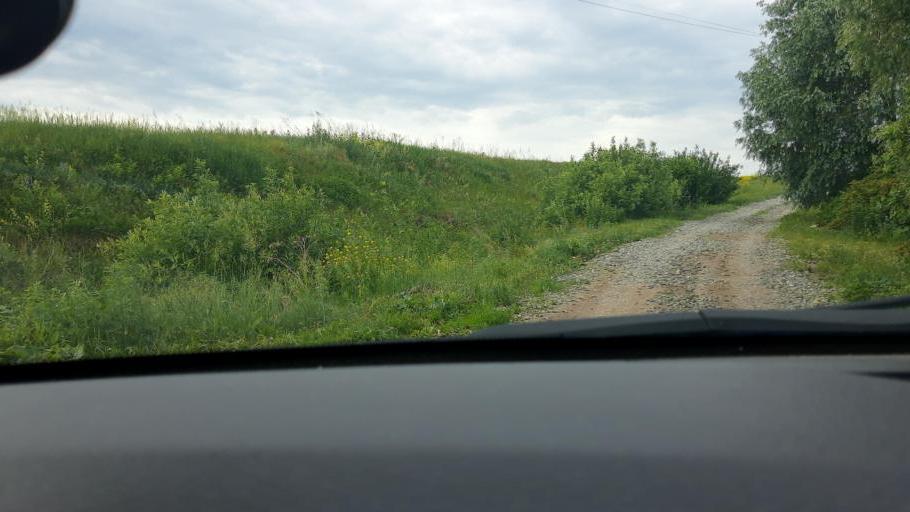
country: RU
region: Bashkortostan
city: Avdon
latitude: 54.5992
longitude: 55.7889
